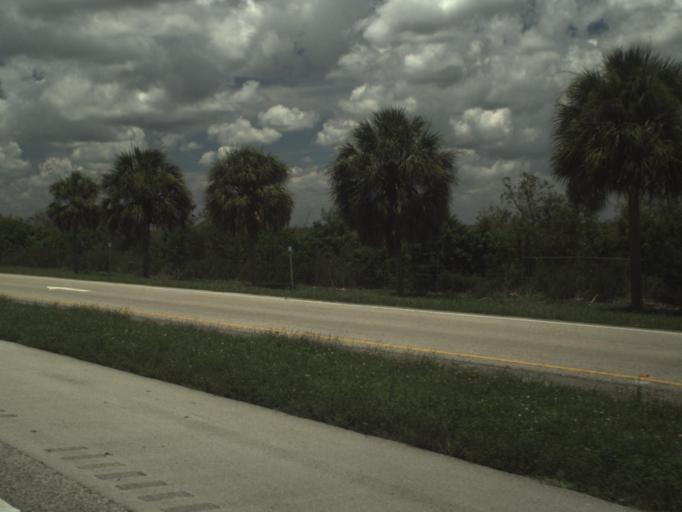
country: US
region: Florida
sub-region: Broward County
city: Weston
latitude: 26.1466
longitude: -80.6414
